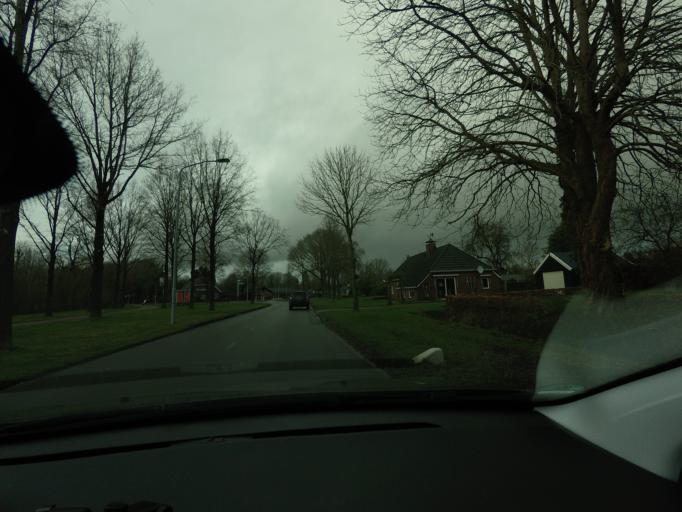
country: NL
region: Drenthe
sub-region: Gemeente Aa en Hunze
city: Anloo
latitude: 53.0020
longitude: 6.7544
